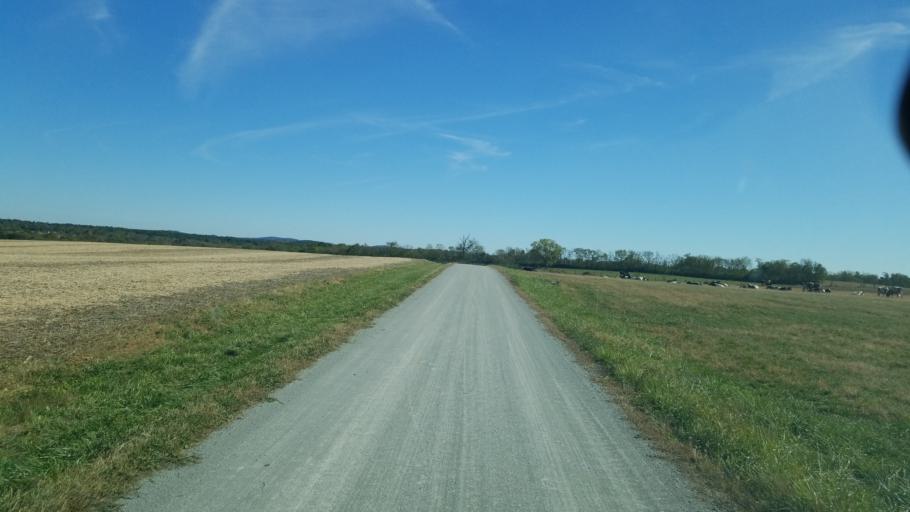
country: US
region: Ohio
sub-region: Highland County
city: Leesburg
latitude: 39.2942
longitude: -83.4729
